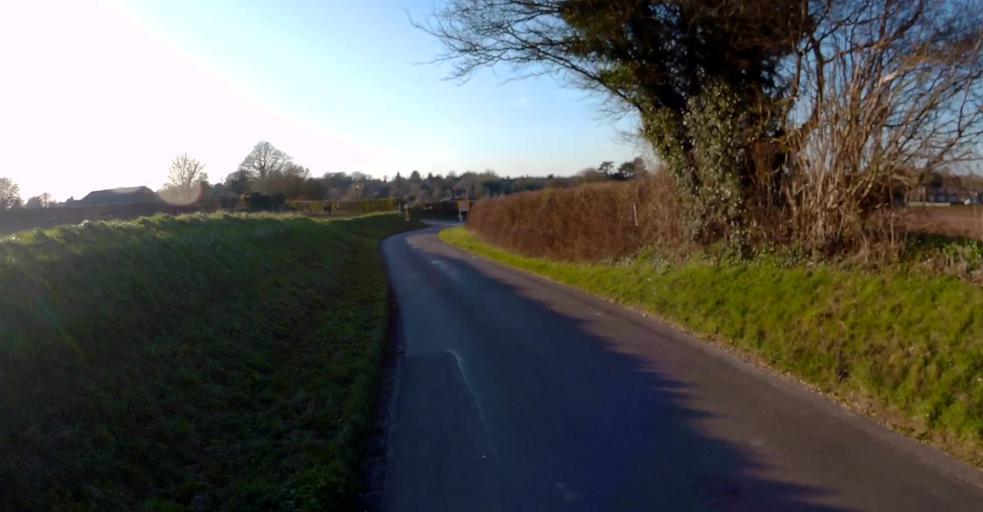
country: GB
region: England
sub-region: Hampshire
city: Basingstoke
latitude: 51.2352
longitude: -1.0931
